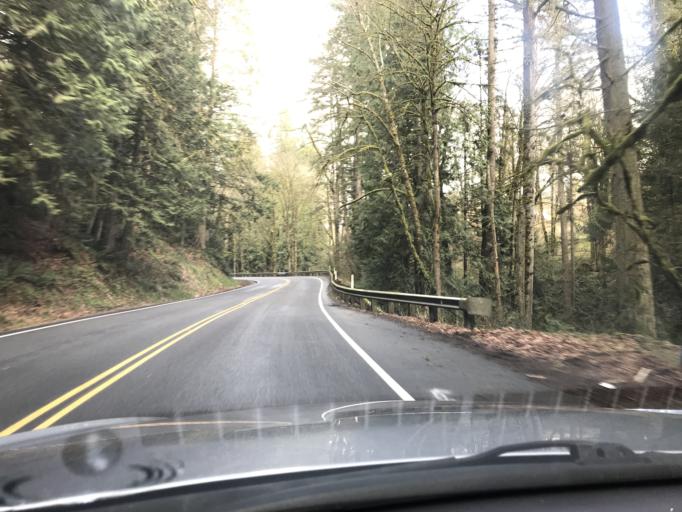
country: US
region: Washington
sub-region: King County
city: Ames Lake
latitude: 47.6336
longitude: -121.9911
